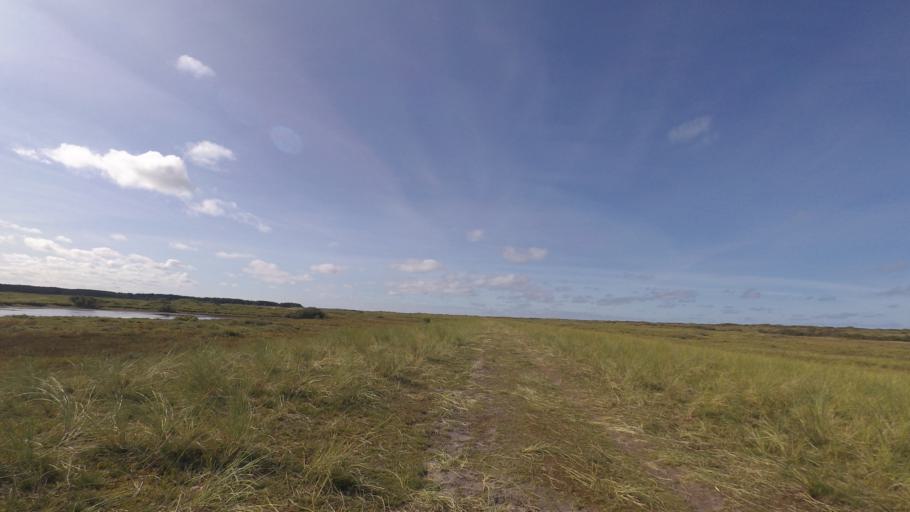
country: NL
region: Friesland
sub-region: Gemeente Ameland
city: Nes
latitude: 53.4537
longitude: 5.7117
